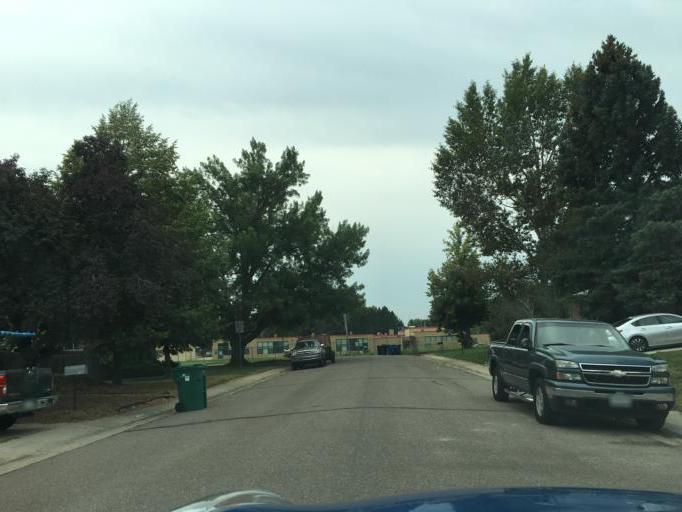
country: US
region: Colorado
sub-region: Jefferson County
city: Wheat Ridge
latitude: 39.7536
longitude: -105.0938
